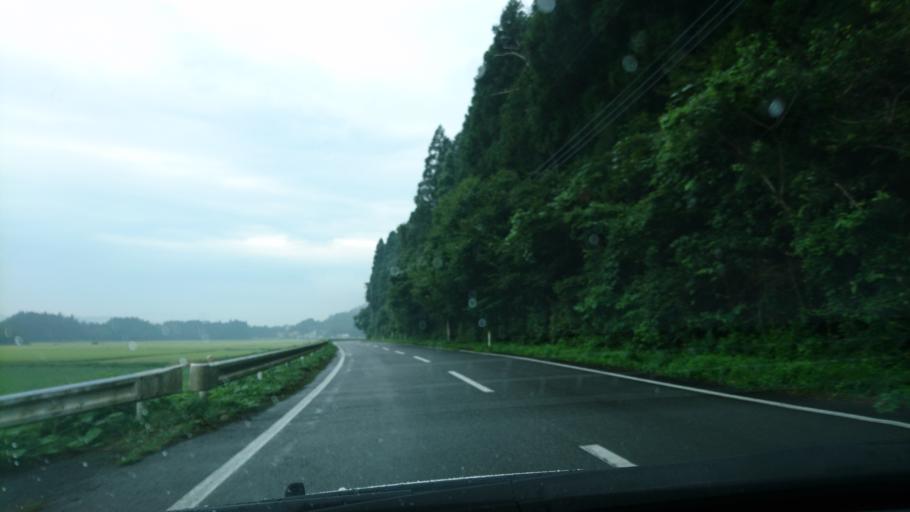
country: JP
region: Iwate
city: Ichinoseki
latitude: 38.8711
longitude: 141.2651
